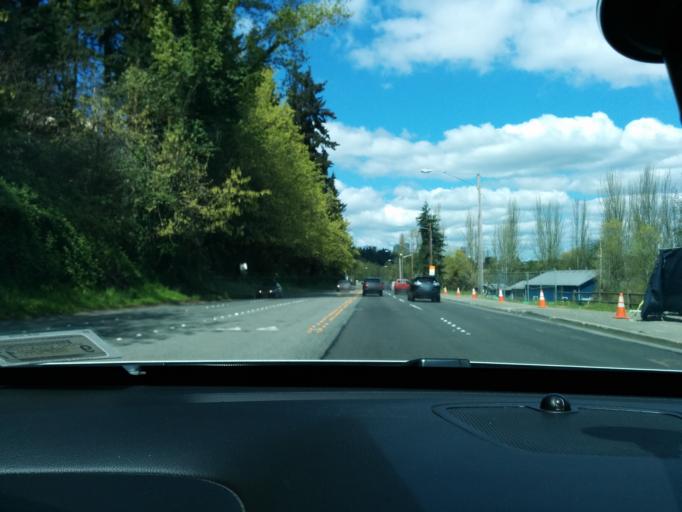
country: US
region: Washington
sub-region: King County
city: Newport
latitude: 47.5874
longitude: -122.1915
